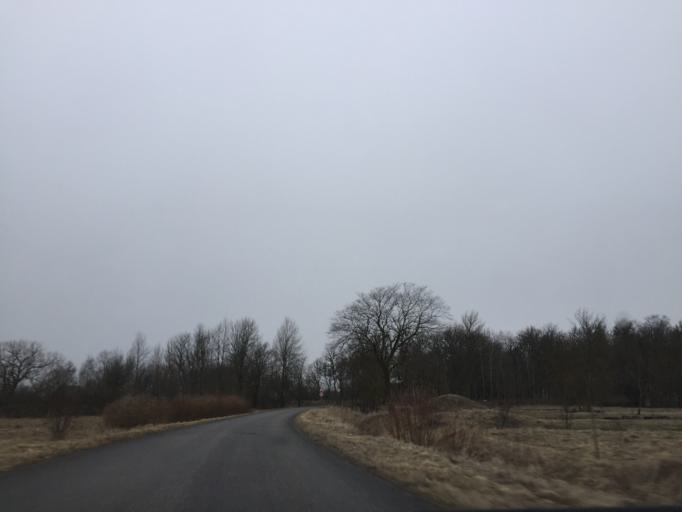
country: EE
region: Laeaene
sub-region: Lihula vald
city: Lihula
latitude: 58.6485
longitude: 23.6178
